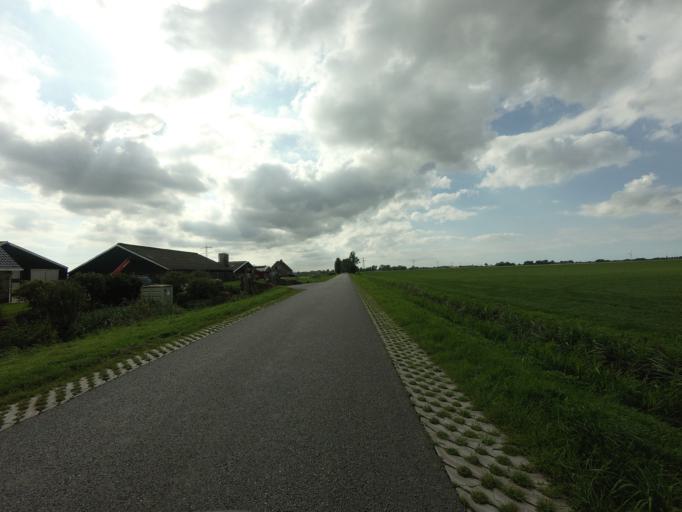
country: NL
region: Friesland
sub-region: Gemeente Littenseradiel
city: Wommels
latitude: 53.0699
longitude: 5.5883
